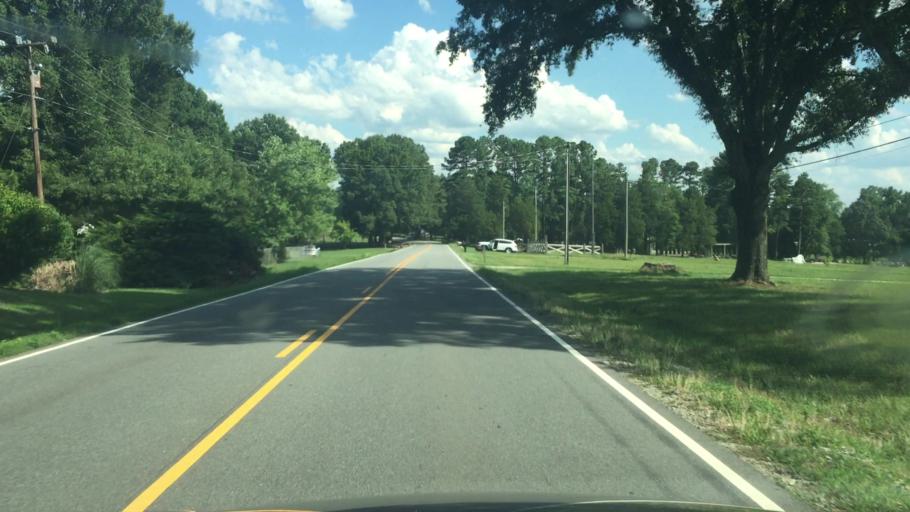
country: US
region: North Carolina
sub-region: Rowan County
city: Enochville
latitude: 35.4654
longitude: -80.7402
